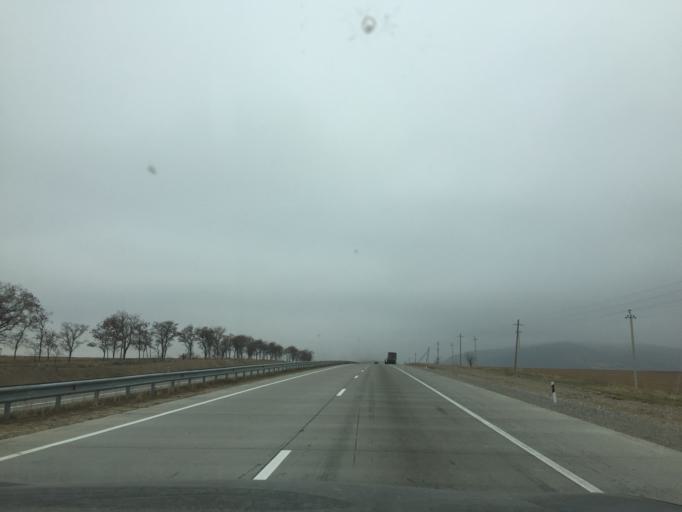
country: KZ
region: Ongtustik Qazaqstan
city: Sastobe
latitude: 42.5204
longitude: 69.9973
